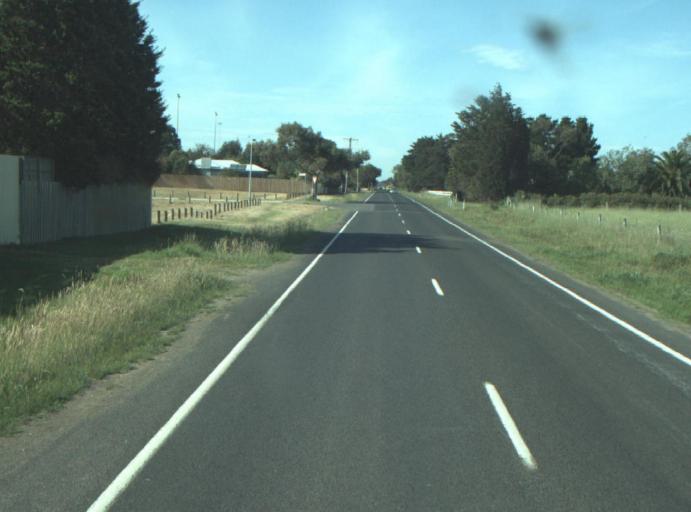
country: AU
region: Victoria
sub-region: Greater Geelong
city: Leopold
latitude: -38.1805
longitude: 144.4568
